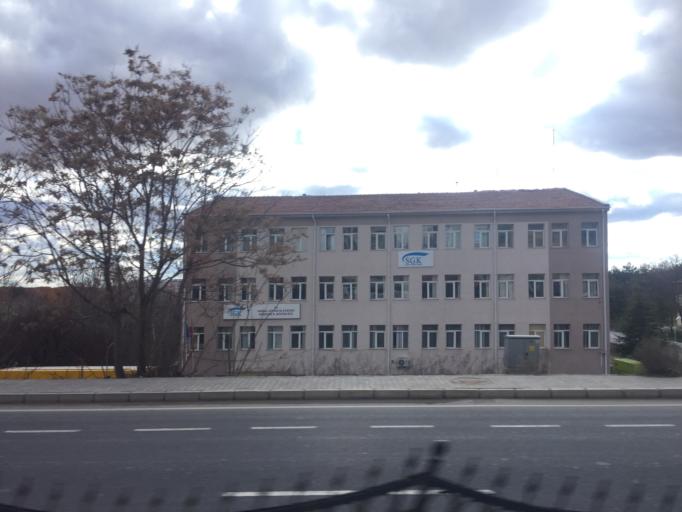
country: TR
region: Kirsehir
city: Kirsehir
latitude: 39.1622
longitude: 34.1579
